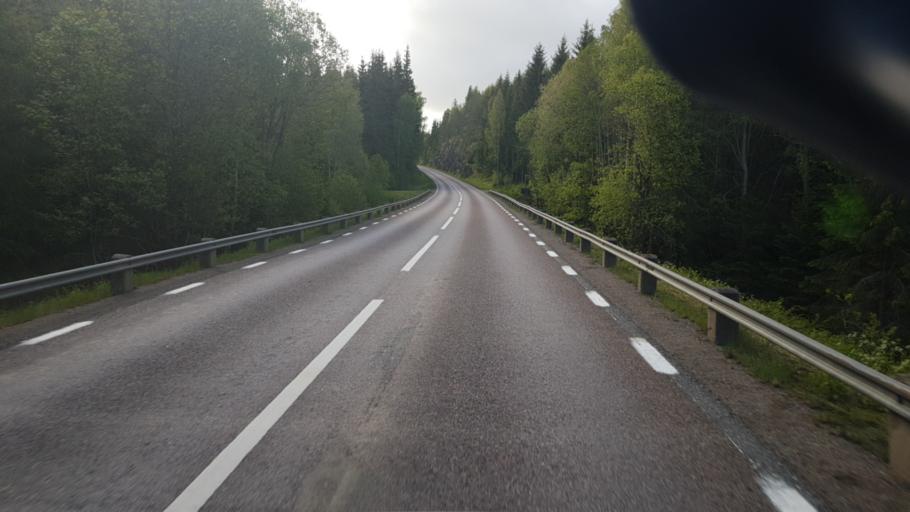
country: SE
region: Vaermland
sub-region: Eda Kommun
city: Amotfors
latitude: 59.7298
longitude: 12.2277
